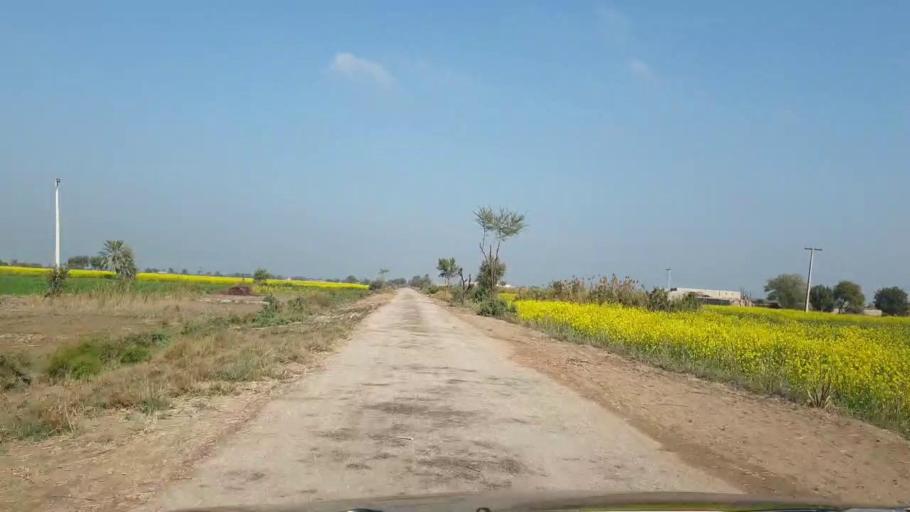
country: PK
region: Sindh
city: Sinjhoro
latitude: 26.0551
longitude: 68.7728
